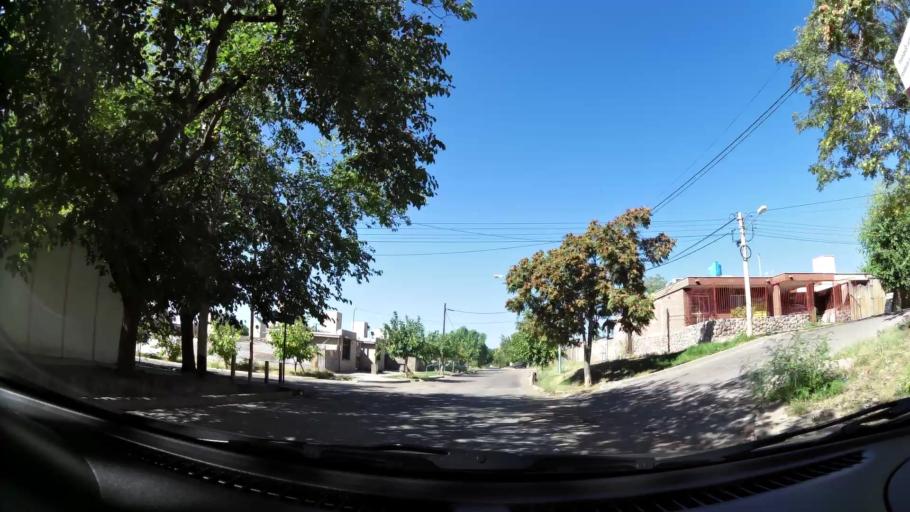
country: AR
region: Mendoza
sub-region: Departamento de Godoy Cruz
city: Godoy Cruz
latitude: -32.9041
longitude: -68.8823
